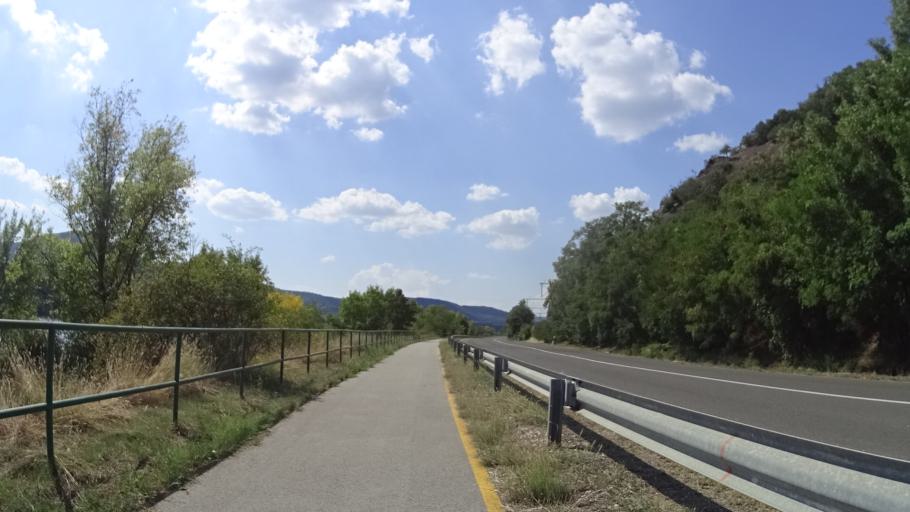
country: HU
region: Pest
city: Nagymaros
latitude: 47.7675
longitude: 18.9266
